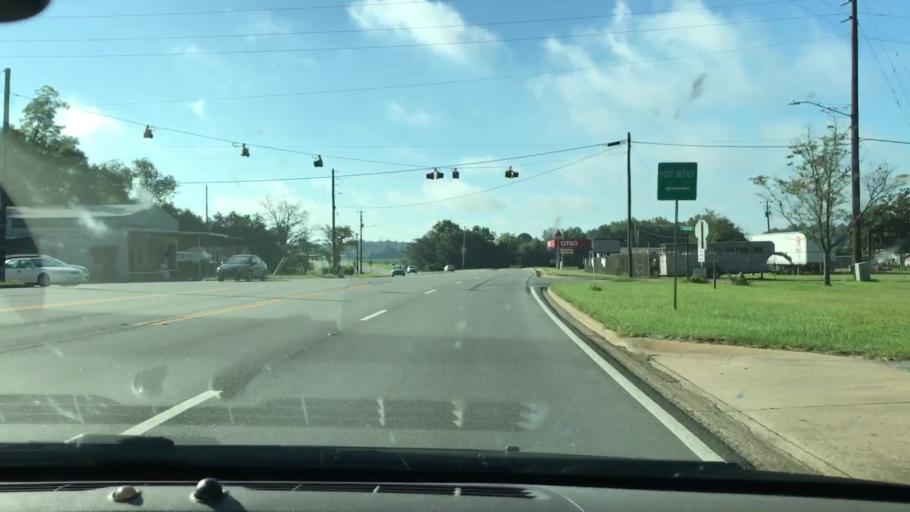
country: US
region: Georgia
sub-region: Terrell County
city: Dawson
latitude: 31.7197
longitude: -84.3489
